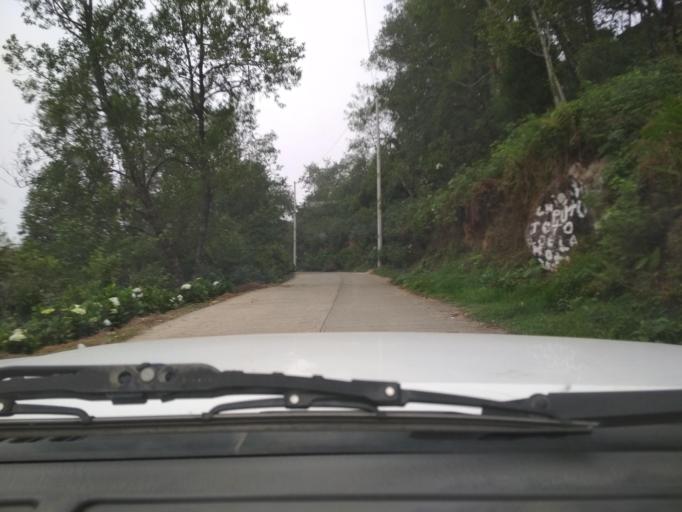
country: MX
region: Veracruz
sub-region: La Perla
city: Metlac Hernandez (Metlac Primero)
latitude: 18.9703
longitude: -97.1417
